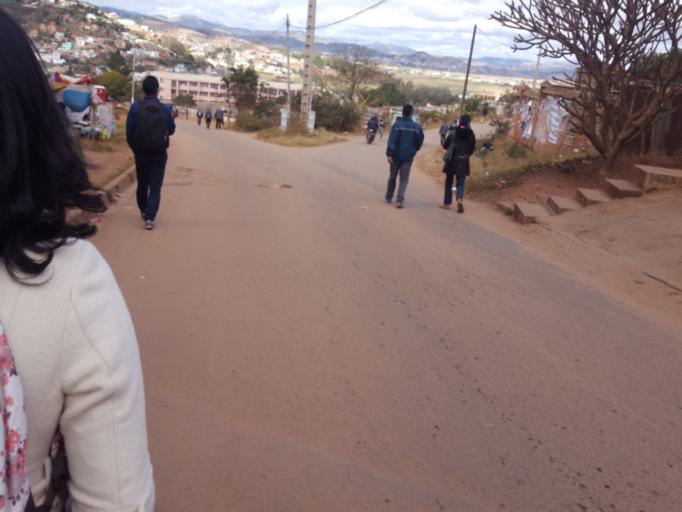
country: MG
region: Analamanga
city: Antananarivo
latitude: -18.9195
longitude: 47.5541
